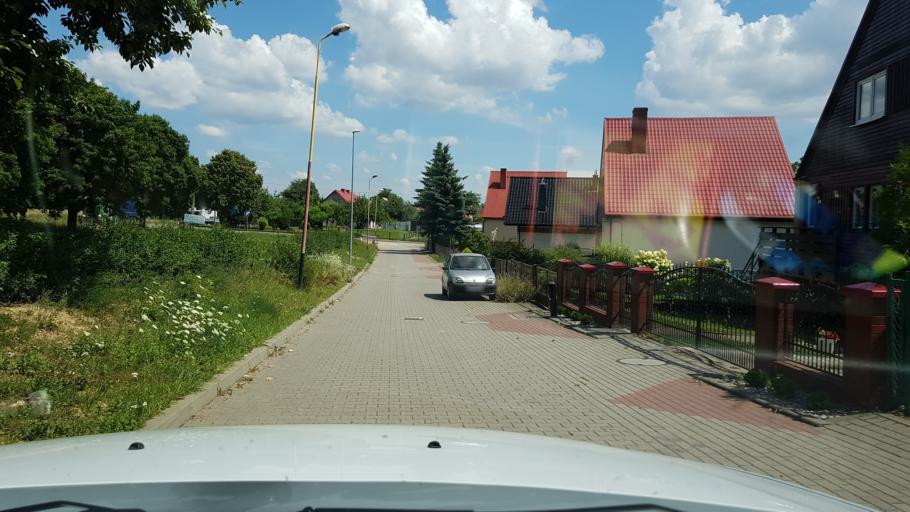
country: PL
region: West Pomeranian Voivodeship
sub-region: Powiat stargardzki
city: Dobrzany
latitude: 53.2725
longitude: 15.4558
